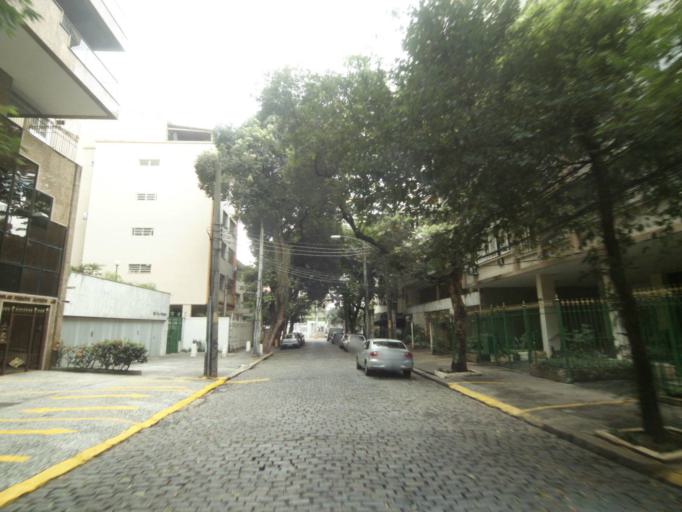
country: BR
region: Rio de Janeiro
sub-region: Rio De Janeiro
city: Rio de Janeiro
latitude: -22.9319
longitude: -43.2452
